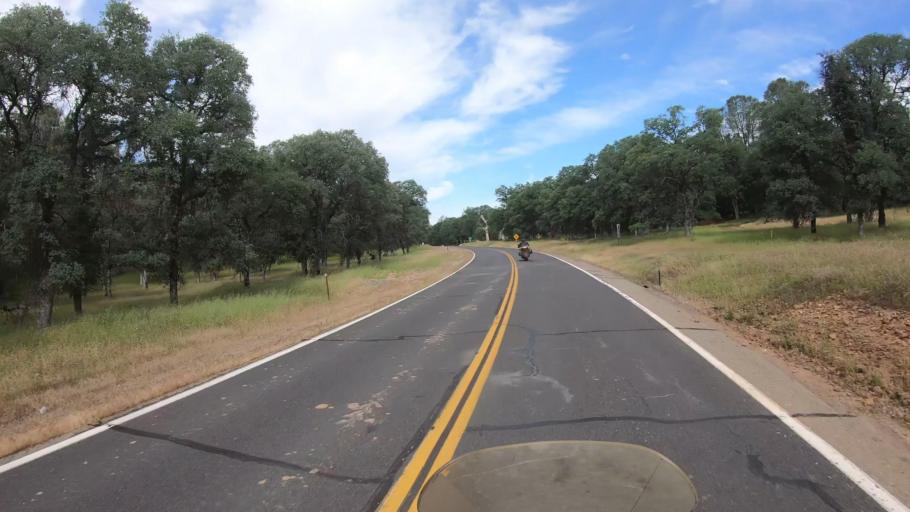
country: US
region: California
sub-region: Tuolumne County
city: Tuolumne City
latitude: 37.8581
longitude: -120.1766
